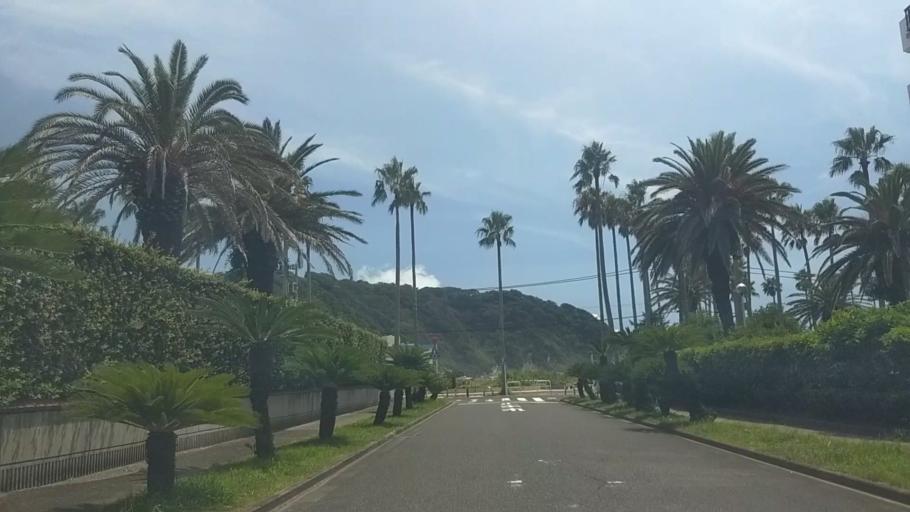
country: JP
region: Kanagawa
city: Kamakura
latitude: 35.2964
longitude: 139.5543
